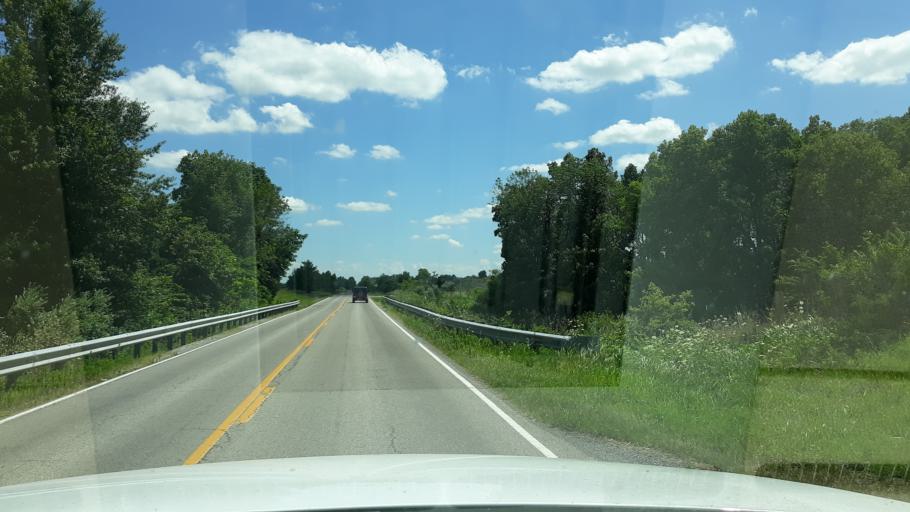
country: US
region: Illinois
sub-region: Saline County
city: Harrisburg
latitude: 37.8622
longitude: -88.6056
